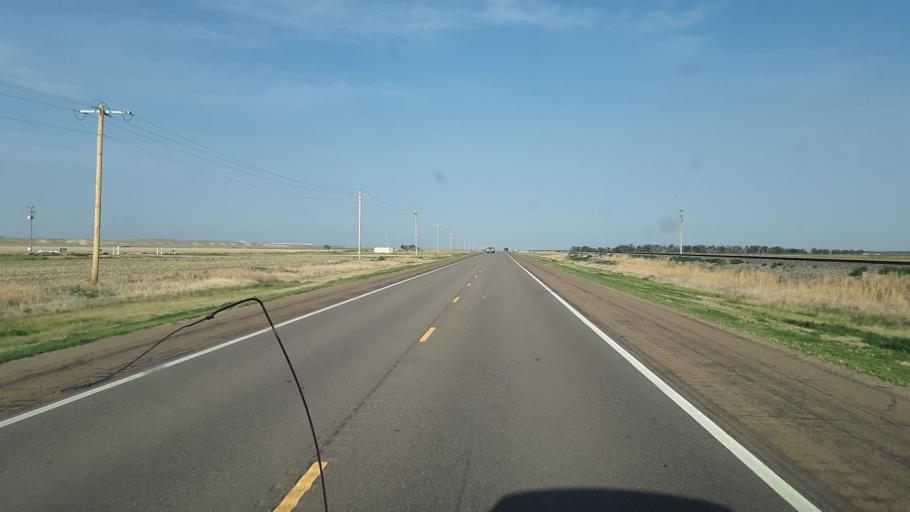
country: US
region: Kansas
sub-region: Hamilton County
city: Syracuse
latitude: 38.0348
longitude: -101.9840
